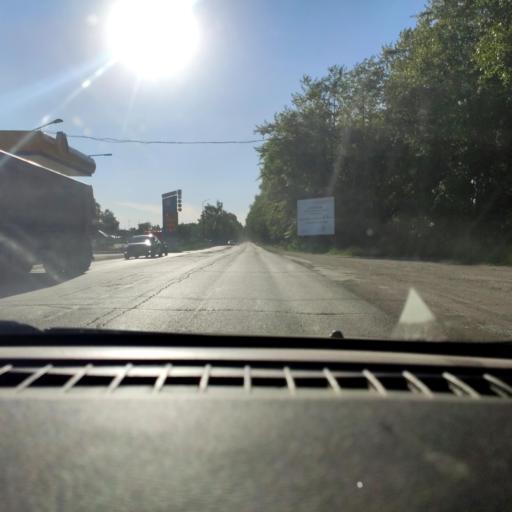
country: RU
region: Perm
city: Overyata
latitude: 58.0599
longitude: 55.8260
